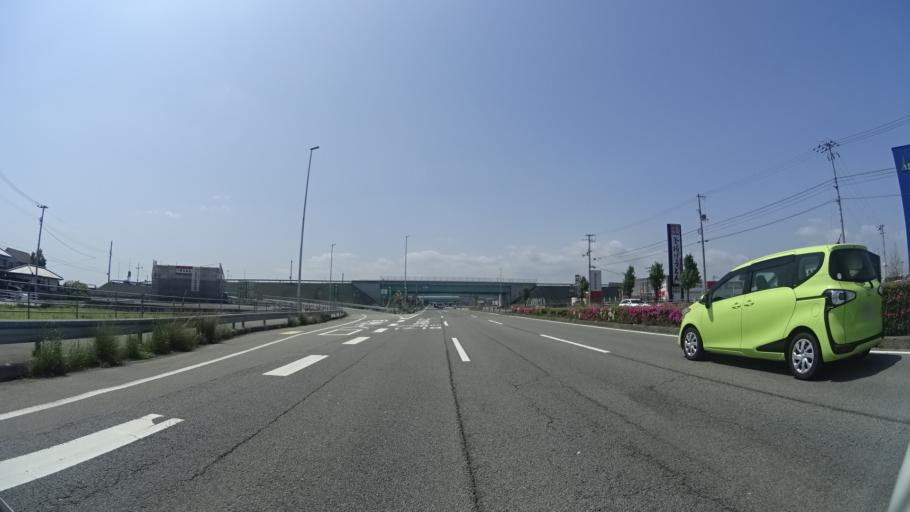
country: JP
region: Tokushima
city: Tokushima-shi
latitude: 34.1051
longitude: 134.5762
